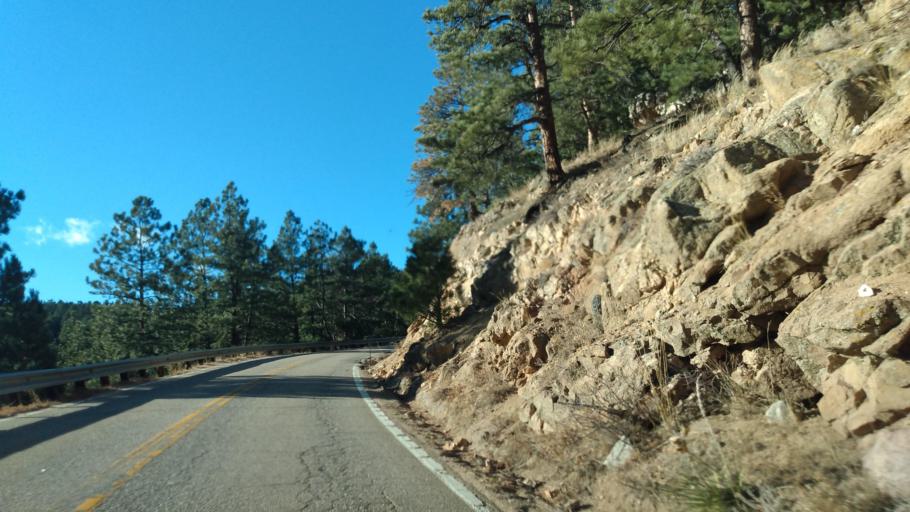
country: US
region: Colorado
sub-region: Boulder County
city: Boulder
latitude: 39.9959
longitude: -105.3578
